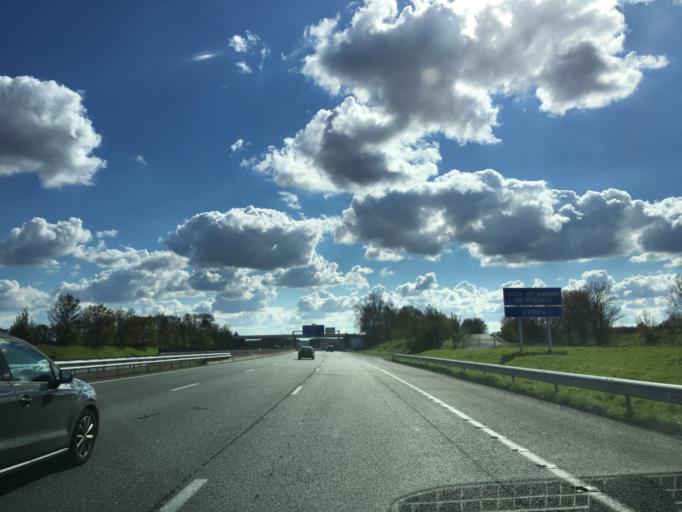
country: FR
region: Nord-Pas-de-Calais
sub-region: Departement du Pas-de-Calais
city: Biache-Saint-Vaast
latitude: 50.3396
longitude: 2.9279
